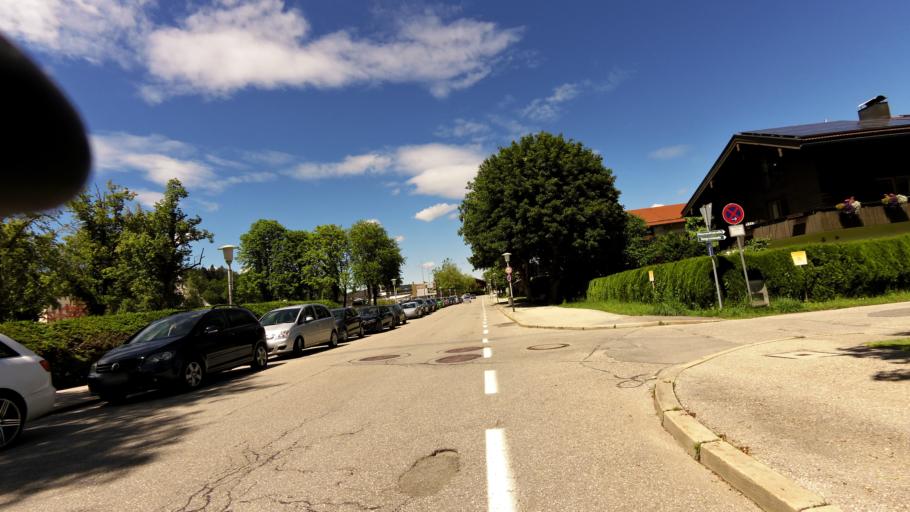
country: DE
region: Bavaria
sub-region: Upper Bavaria
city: Bad Wiessee
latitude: 47.7175
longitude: 11.7248
